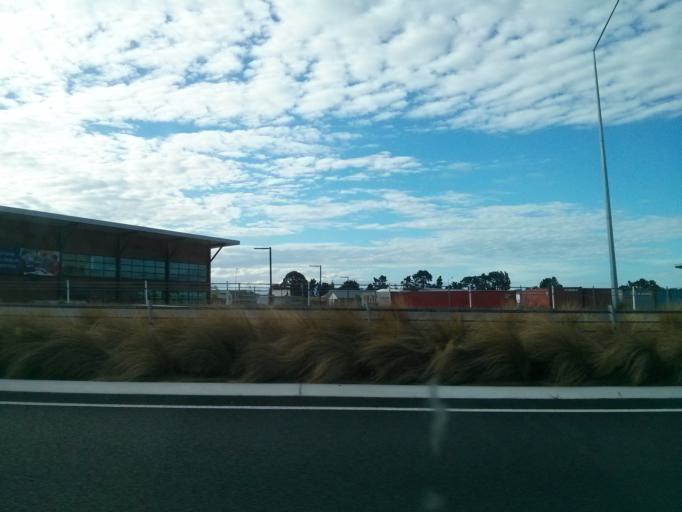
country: NZ
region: Canterbury
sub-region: Christchurch City
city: Christchurch
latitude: -43.4739
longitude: 172.5610
